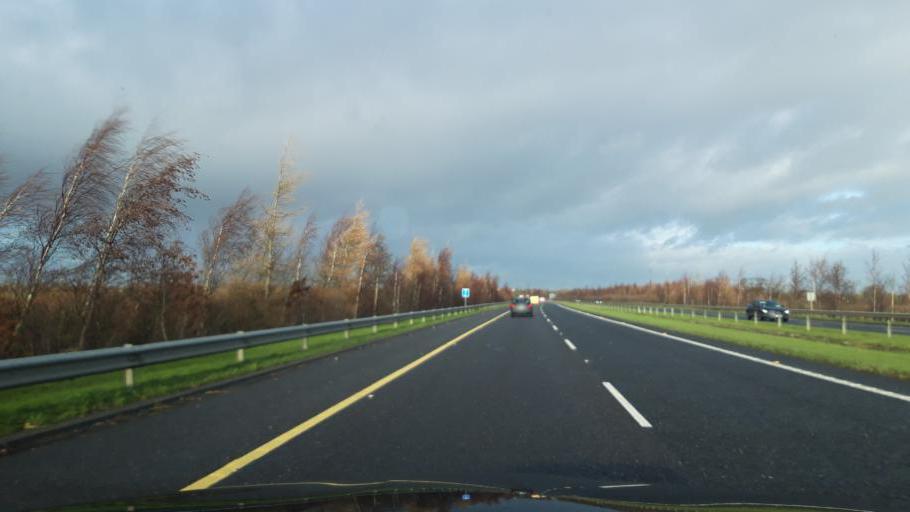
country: IE
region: Leinster
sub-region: Fingal County
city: Blanchardstown
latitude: 53.4494
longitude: -6.3554
